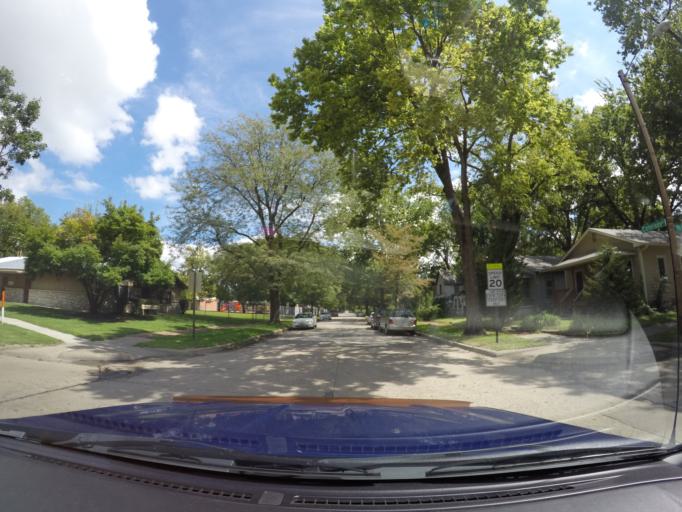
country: US
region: Kansas
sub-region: Riley County
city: Manhattan
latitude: 39.1763
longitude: -96.5685
